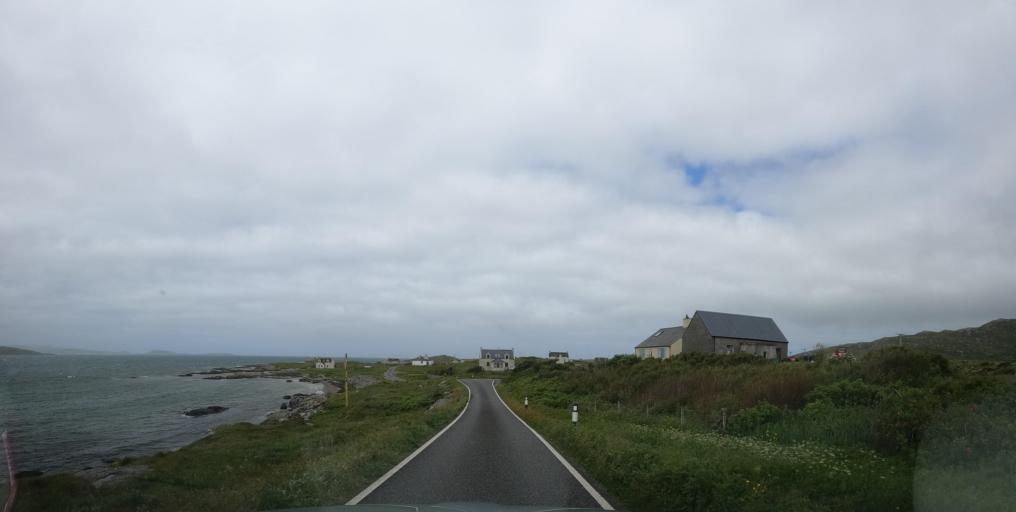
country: GB
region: Scotland
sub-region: Eilean Siar
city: Isle of South Uist
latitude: 57.1034
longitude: -7.3338
